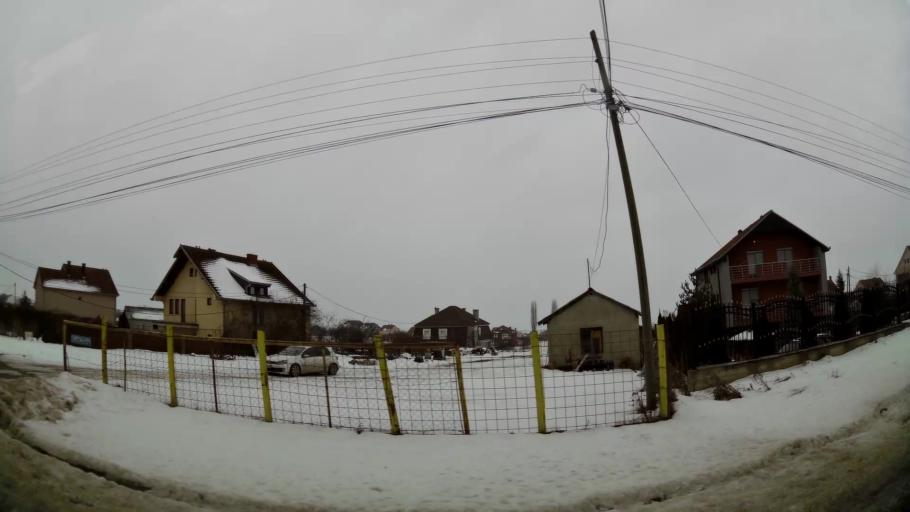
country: XK
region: Pristina
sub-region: Komuna e Prishtines
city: Pristina
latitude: 42.7227
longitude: 21.1463
